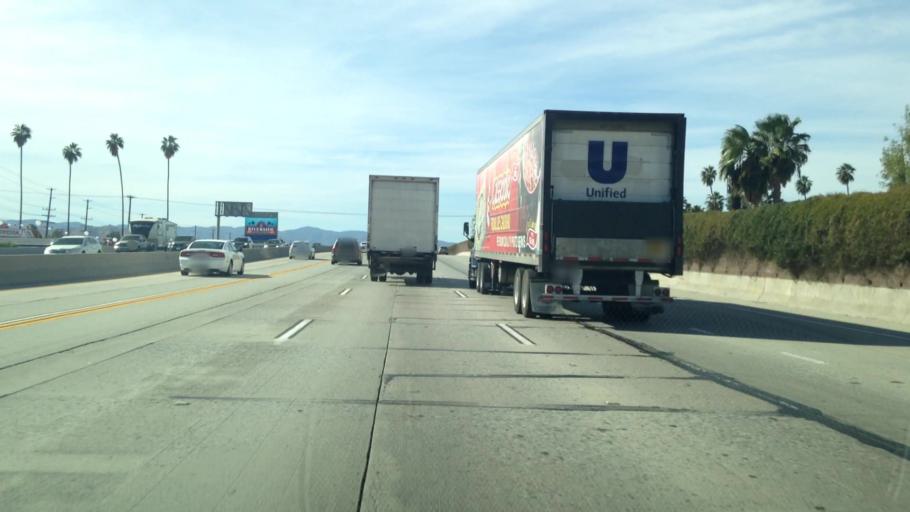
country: US
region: California
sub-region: Riverside County
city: Riverside
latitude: 33.9328
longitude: -117.4106
